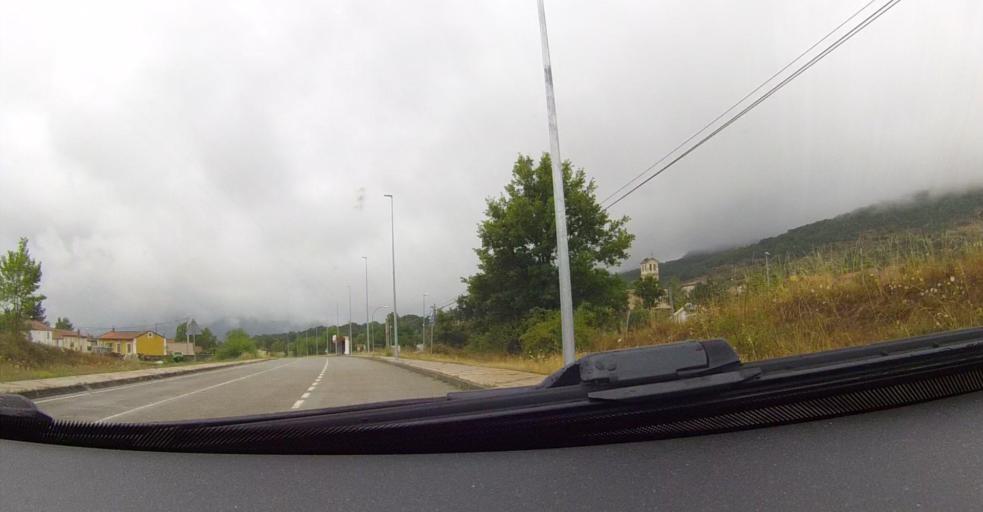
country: ES
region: Castille and Leon
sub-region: Provincia de Leon
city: Bonar
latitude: 42.8495
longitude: -5.2749
